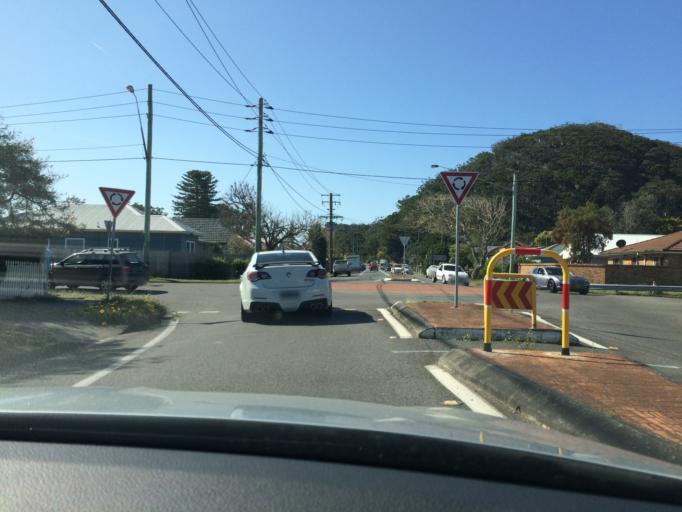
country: AU
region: New South Wales
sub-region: Gosford Shire
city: Ettalong Beach
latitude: -33.5120
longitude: 151.3305
